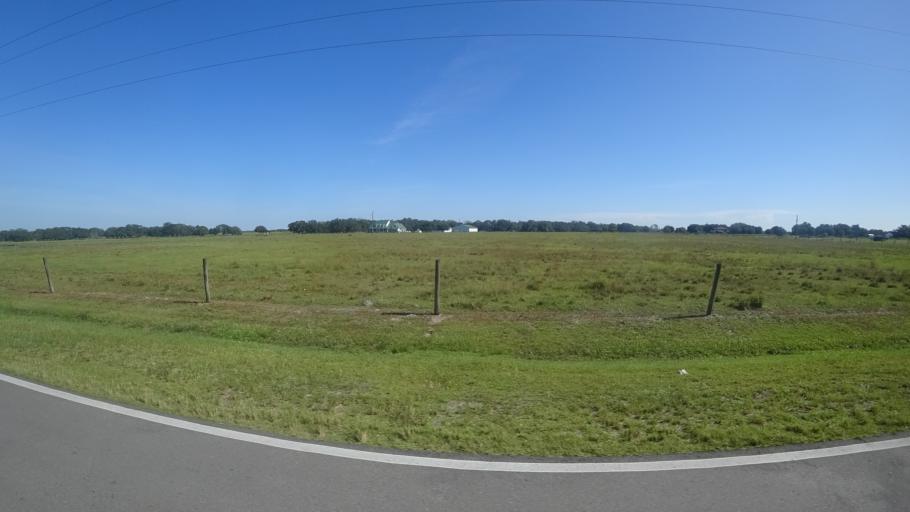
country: US
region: Florida
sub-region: Sarasota County
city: Warm Mineral Springs
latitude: 27.2789
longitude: -82.2113
